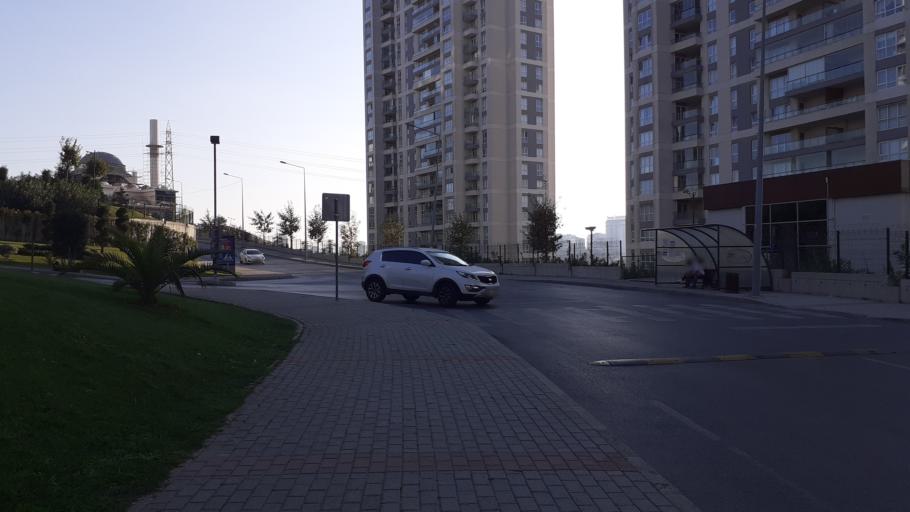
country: TR
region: Istanbul
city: Basaksehir
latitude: 41.0660
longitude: 28.7758
